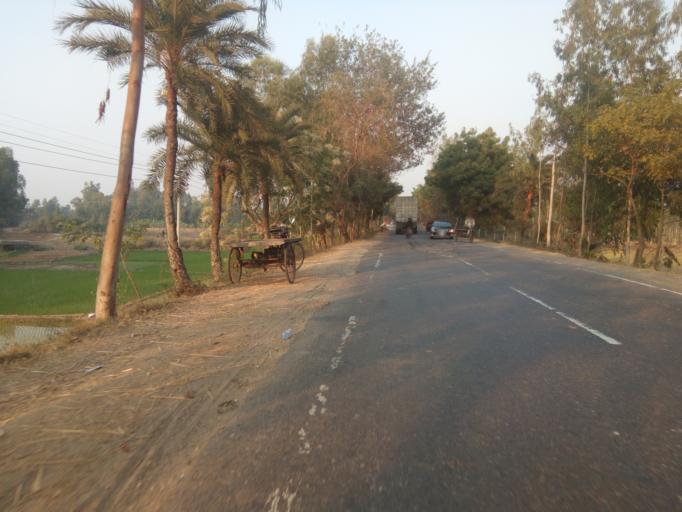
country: BD
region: Rajshahi
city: Par Naogaon
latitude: 24.5420
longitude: 89.1853
